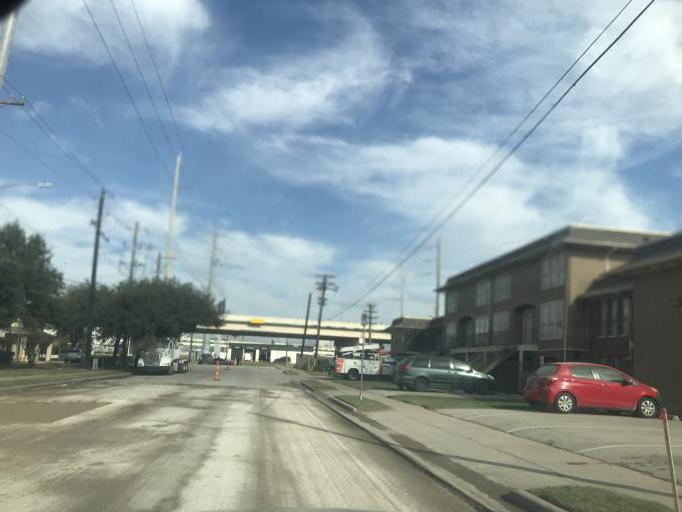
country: US
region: Texas
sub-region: Harris County
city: Bellaire
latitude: 29.7235
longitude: -95.4807
